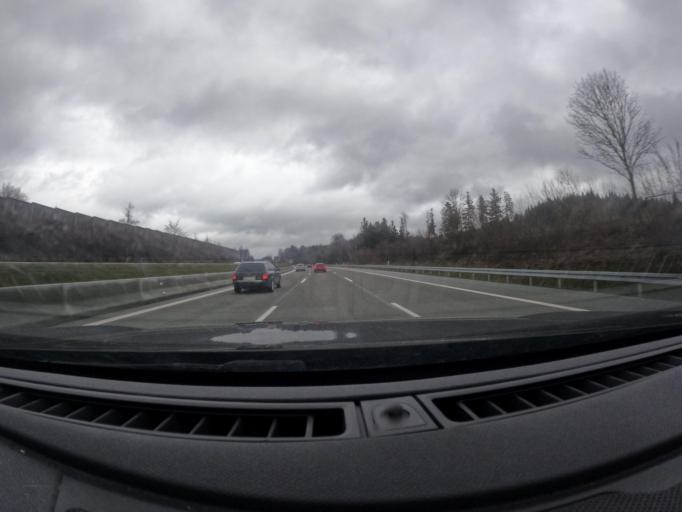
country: DE
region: Bavaria
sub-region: Upper Franconia
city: Marktschorgast
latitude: 50.0767
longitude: 11.6534
